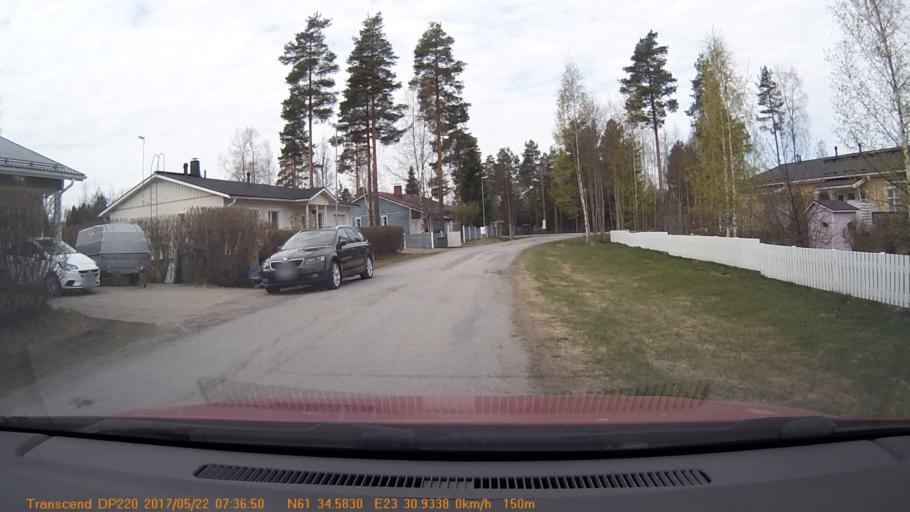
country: FI
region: Pirkanmaa
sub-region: Tampere
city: Yloejaervi
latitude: 61.5764
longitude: 23.5156
